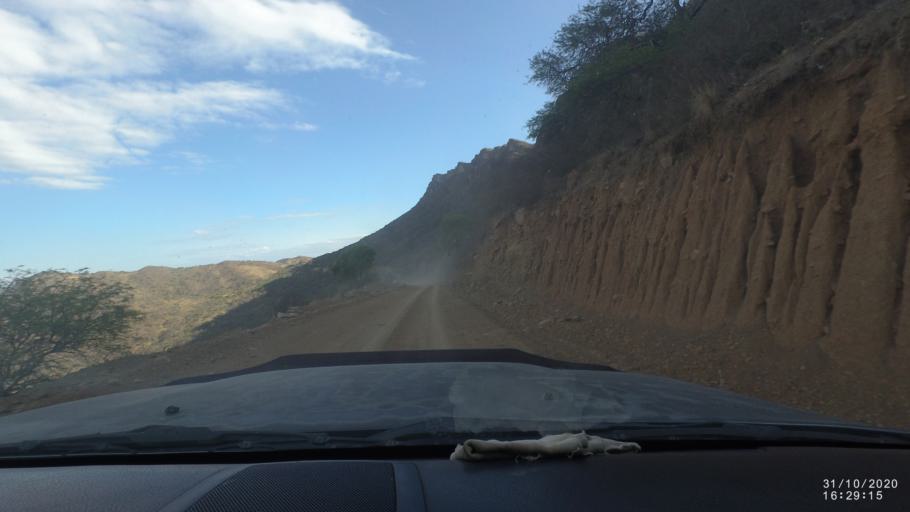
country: BO
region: Chuquisaca
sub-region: Provincia Zudanez
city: Mojocoya
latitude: -18.4186
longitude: -64.5858
